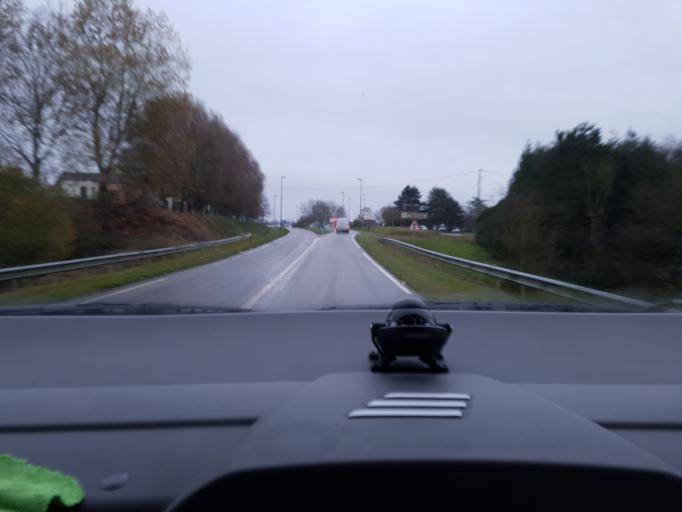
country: FR
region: Haute-Normandie
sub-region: Departement de l'Eure
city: Le Neubourg
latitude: 49.1413
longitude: 0.9006
